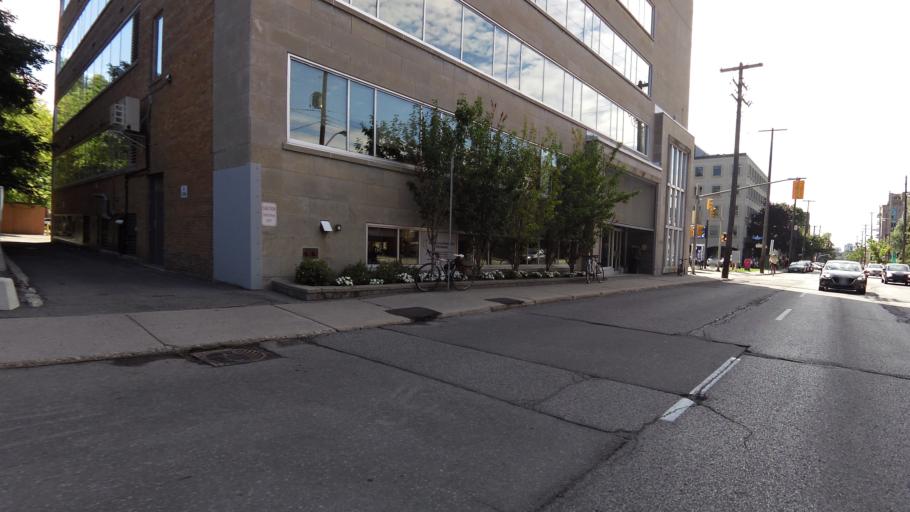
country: CA
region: Ontario
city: Ottawa
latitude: 45.4135
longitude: -75.6977
